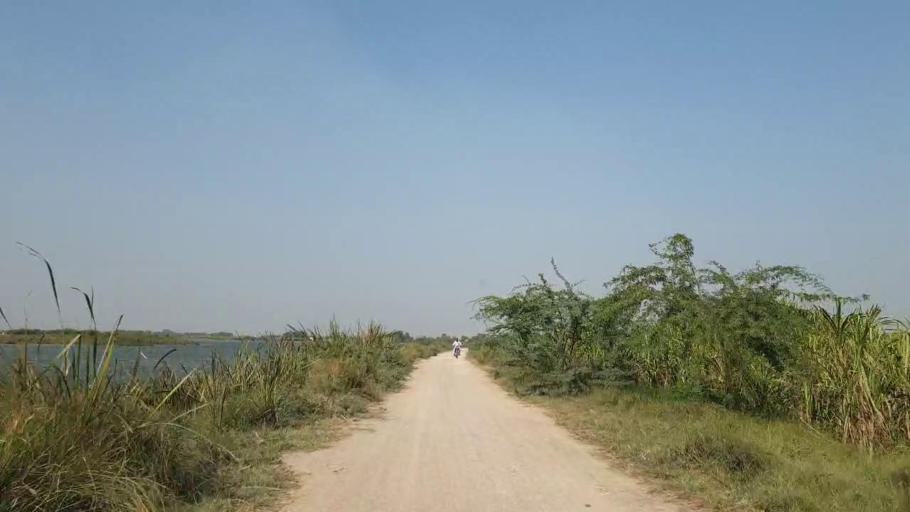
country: PK
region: Sindh
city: Bulri
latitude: 24.9395
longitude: 68.3859
